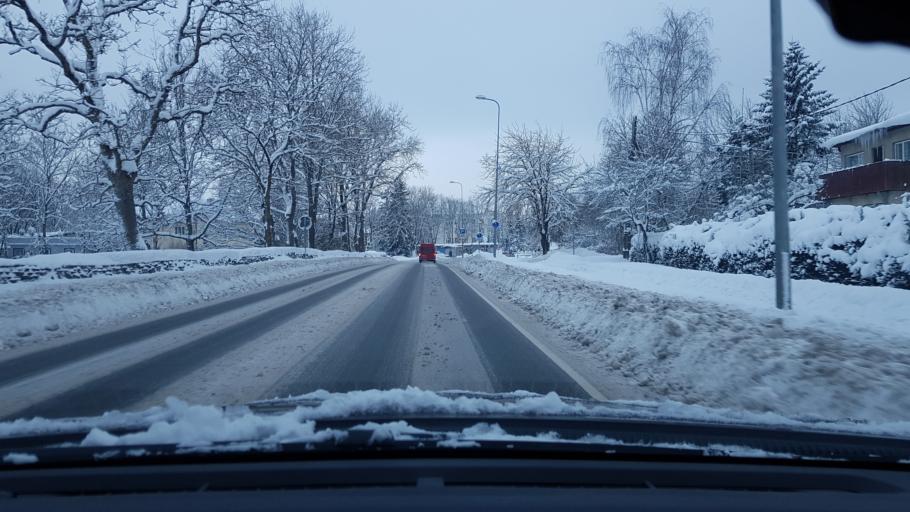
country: EE
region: Harju
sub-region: Saku vald
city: Saku
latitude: 59.3016
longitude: 24.6645
